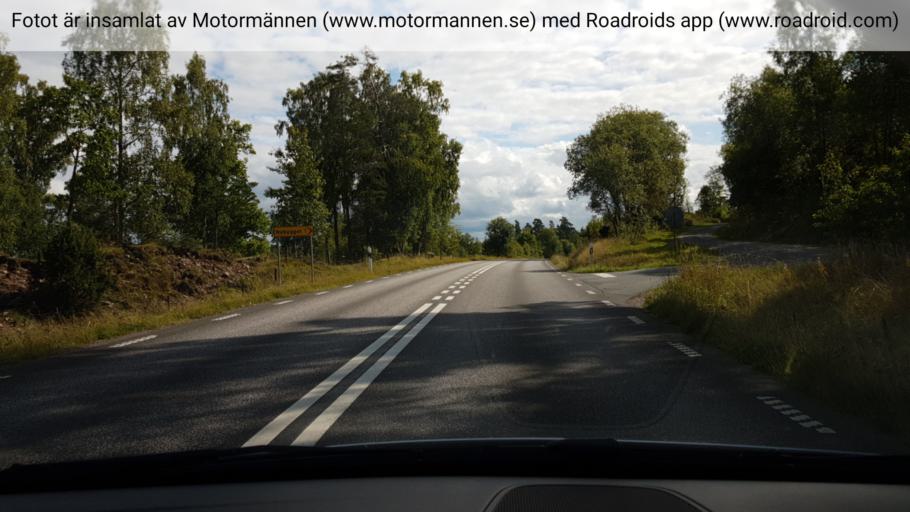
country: SE
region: Joenkoeping
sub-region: Mullsjo Kommun
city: Mullsjoe
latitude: 58.0720
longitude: 13.8043
